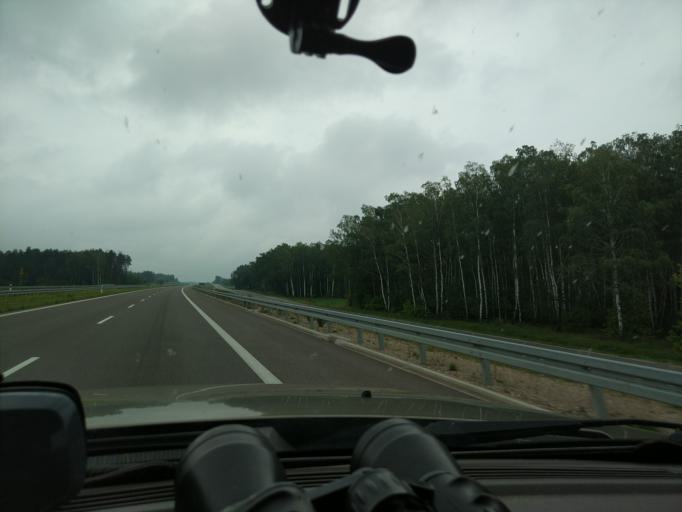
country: PL
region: Podlasie
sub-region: Powiat zambrowski
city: Rutki-Kossaki
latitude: 53.0648
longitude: 22.4110
